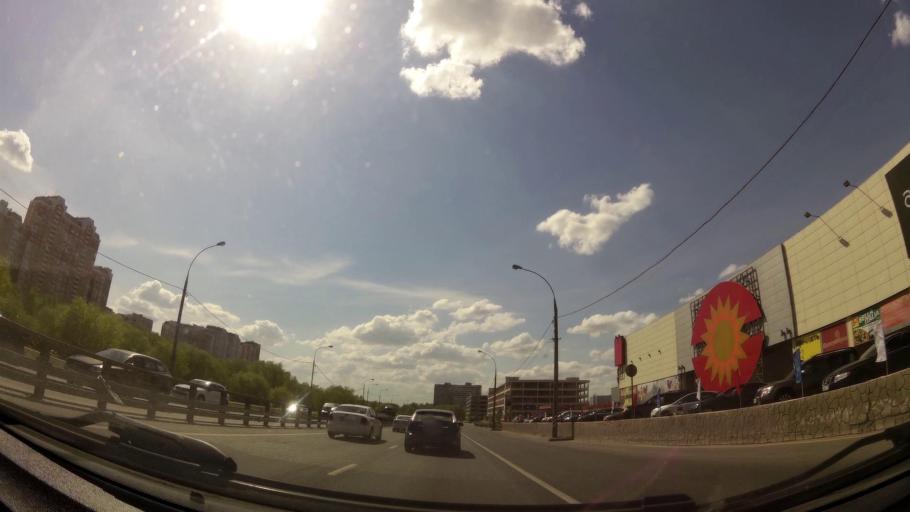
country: RU
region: Moscow
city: Solntsevo
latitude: 55.6582
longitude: 37.4017
